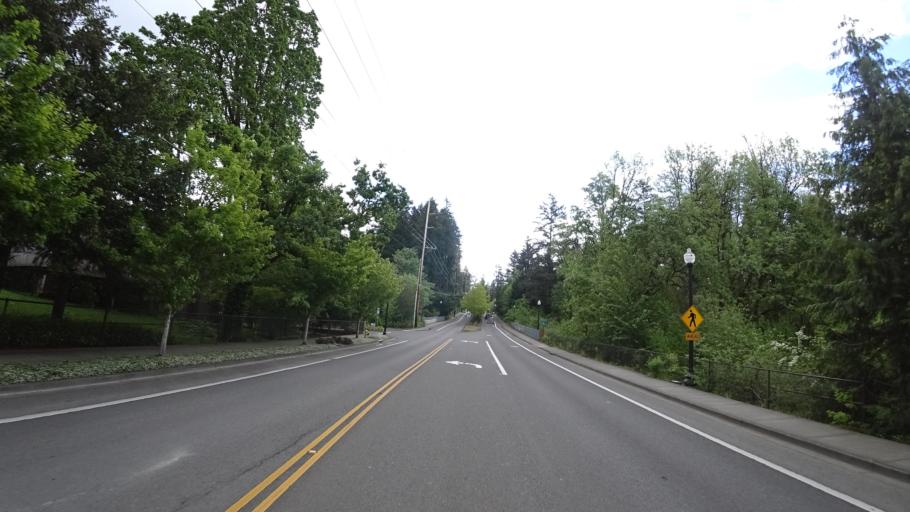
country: US
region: Oregon
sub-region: Washington County
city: Beaverton
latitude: 45.4656
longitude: -122.8352
